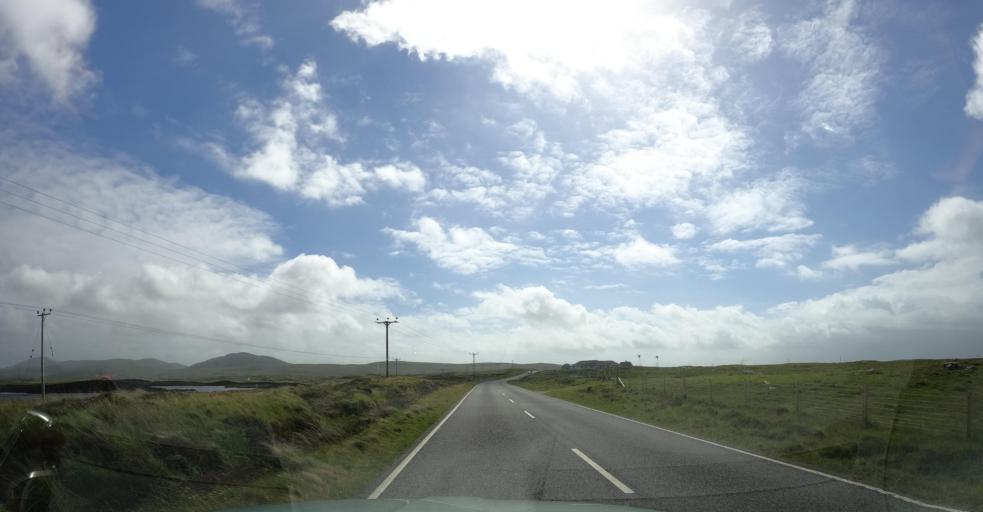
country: GB
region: Scotland
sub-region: Eilean Siar
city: Isle of South Uist
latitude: 57.2532
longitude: -7.3760
